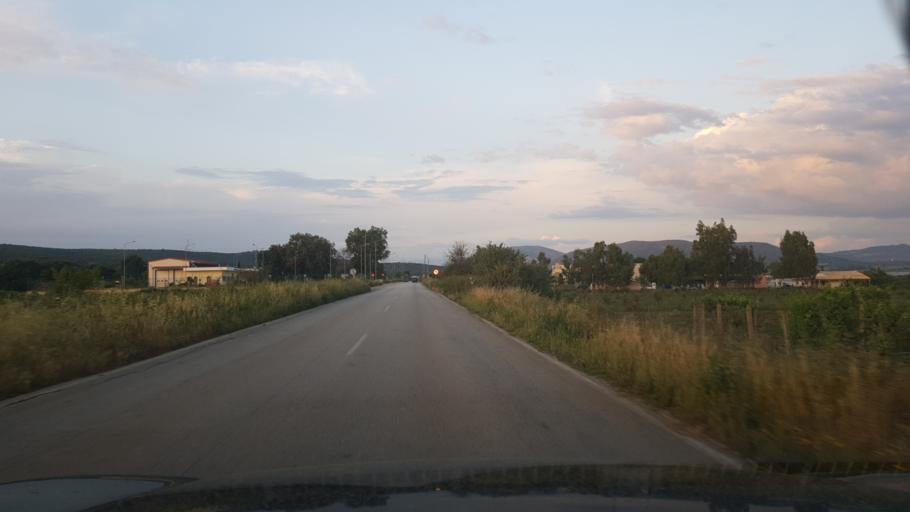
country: GR
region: West Greece
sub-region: Nomos Aitolias kai Akarnanias
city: Vonitsa
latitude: 38.8739
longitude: 20.8154
